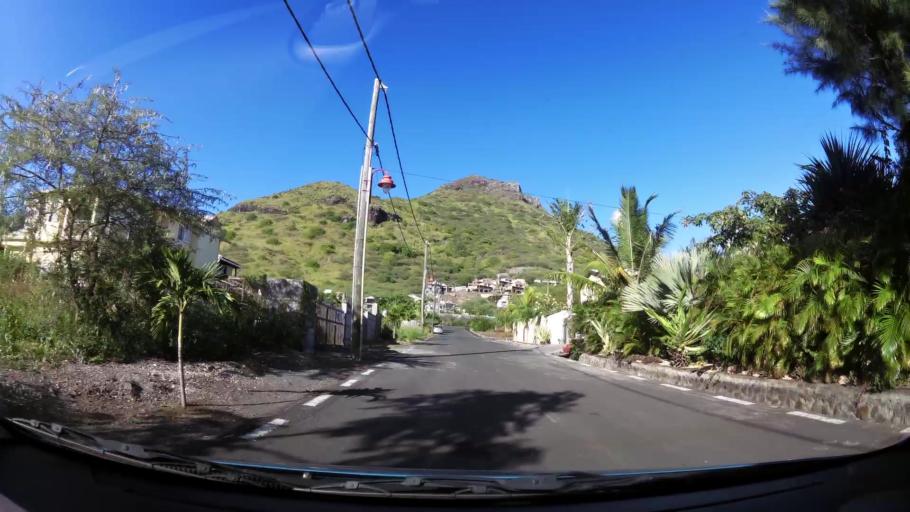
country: MU
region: Black River
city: Tamarin
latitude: -20.3376
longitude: 57.3808
